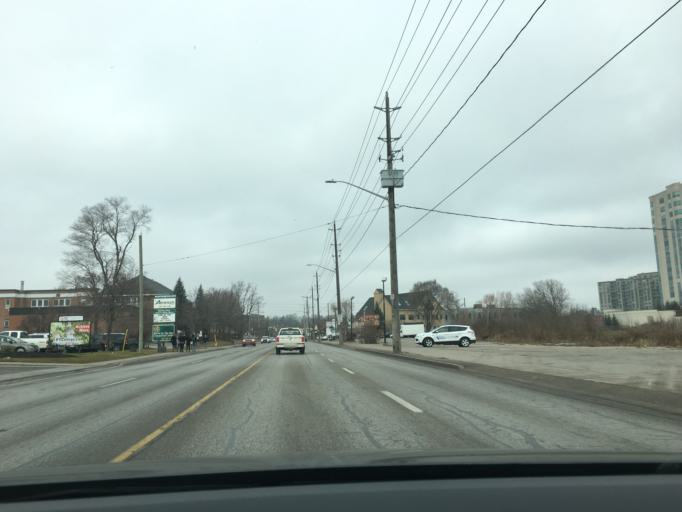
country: CA
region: Ontario
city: Barrie
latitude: 44.3837
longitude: -79.6938
